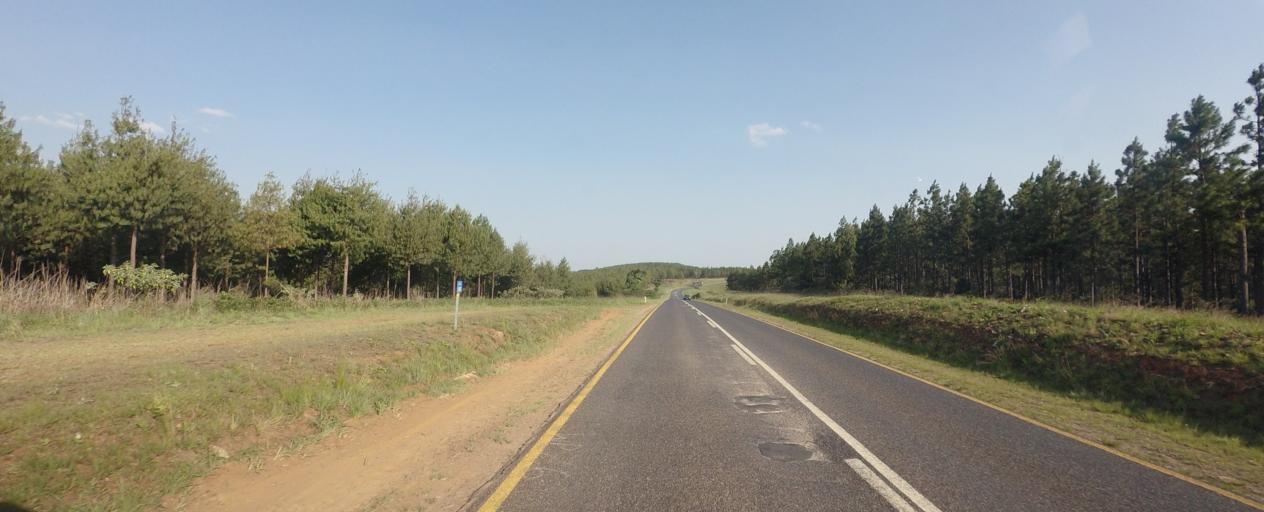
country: ZA
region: Mpumalanga
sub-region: Ehlanzeni District
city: Lydenburg
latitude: -25.1676
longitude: 30.6912
